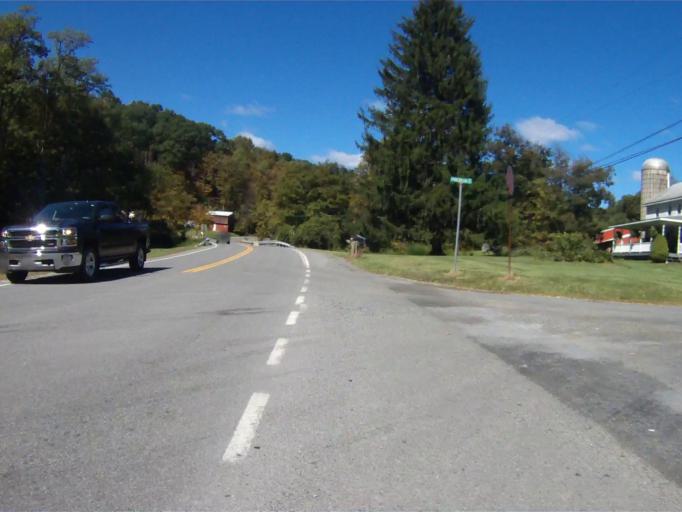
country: US
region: Pennsylvania
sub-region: Centre County
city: Milesburg
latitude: 40.9230
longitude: -77.8988
